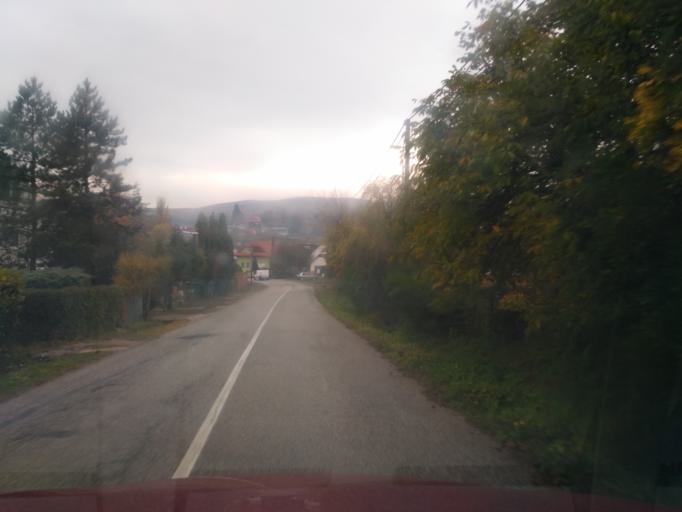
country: SK
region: Kosicky
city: Moldava nad Bodvou
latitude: 48.6738
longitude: 21.1175
